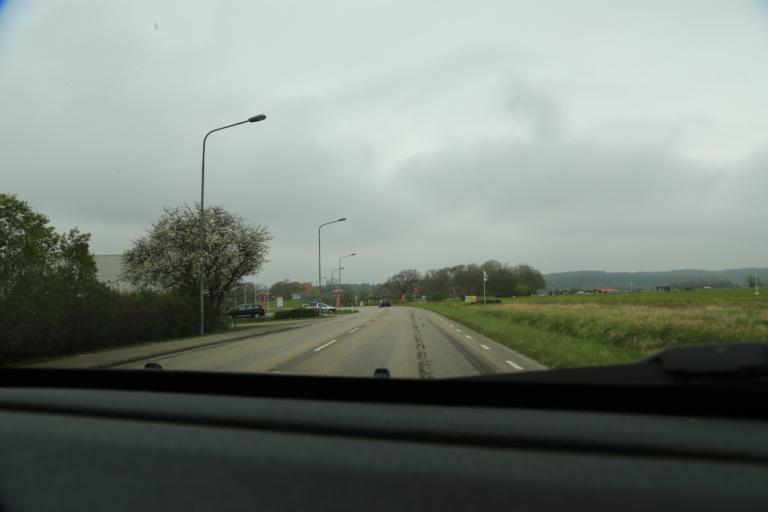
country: SE
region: Halland
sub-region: Varbergs Kommun
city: Veddige
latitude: 57.2212
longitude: 12.2217
